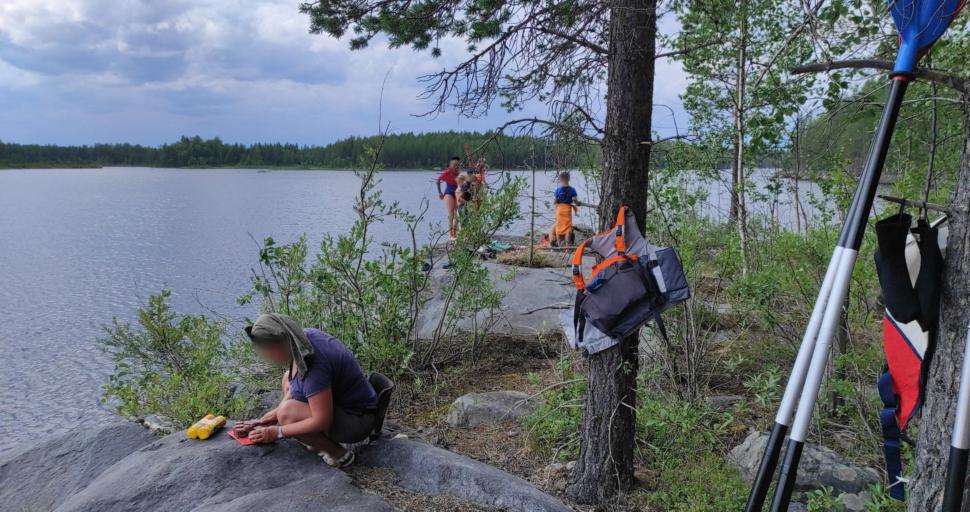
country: RU
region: Murmansk
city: Poyakonda
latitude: 66.6855
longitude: 32.7276
